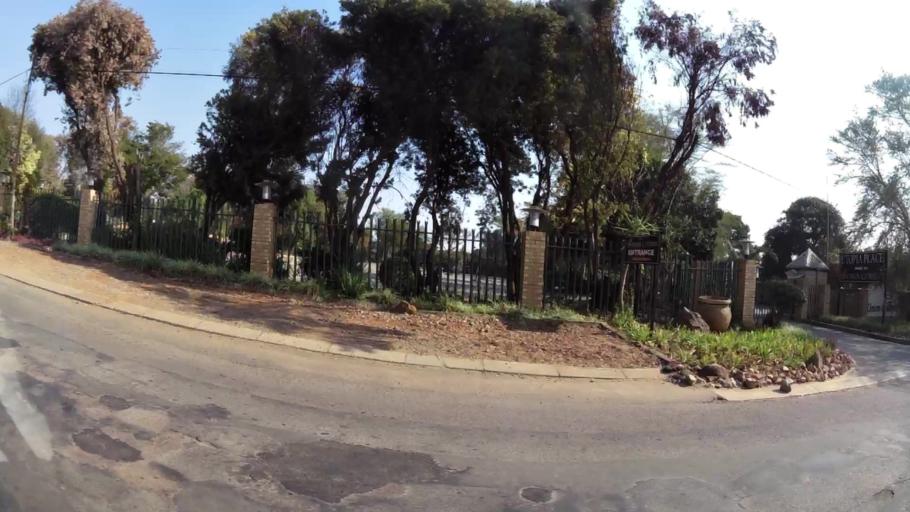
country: ZA
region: Gauteng
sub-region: City of Tshwane Metropolitan Municipality
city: Pretoria
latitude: -25.7724
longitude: 28.3357
